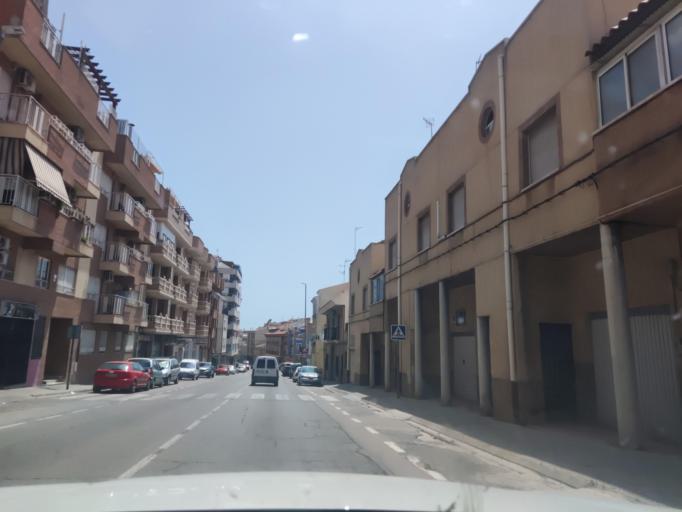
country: ES
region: Castille-La Mancha
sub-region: Provincia de Albacete
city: Hellin
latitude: 38.5139
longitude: -1.6972
